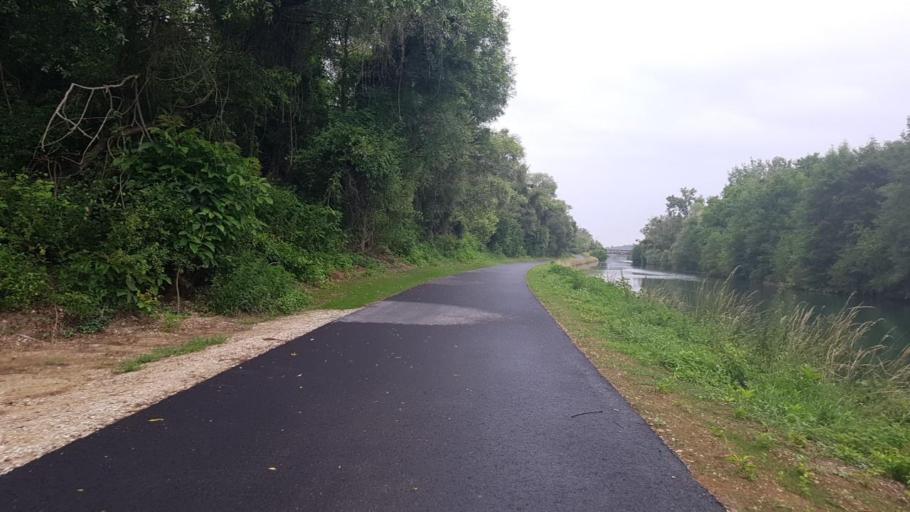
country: FR
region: Champagne-Ardenne
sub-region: Departement de la Marne
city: Vitry-le-Francois
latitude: 48.7774
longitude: 4.5417
